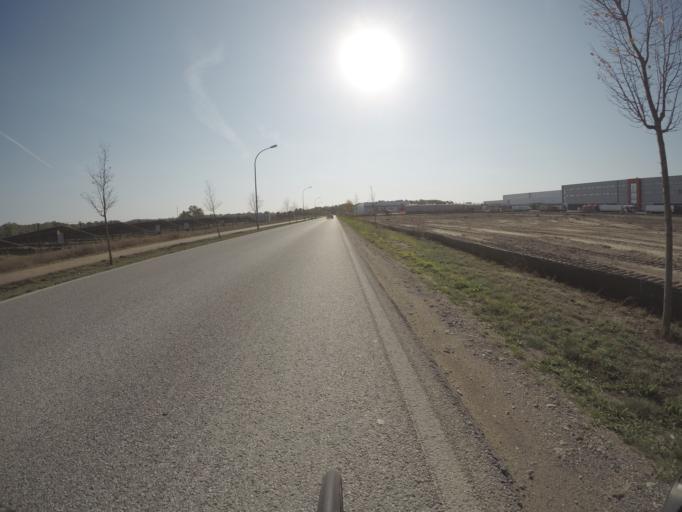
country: DE
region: Brandenburg
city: Leegebruch
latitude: 52.7306
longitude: 13.2203
